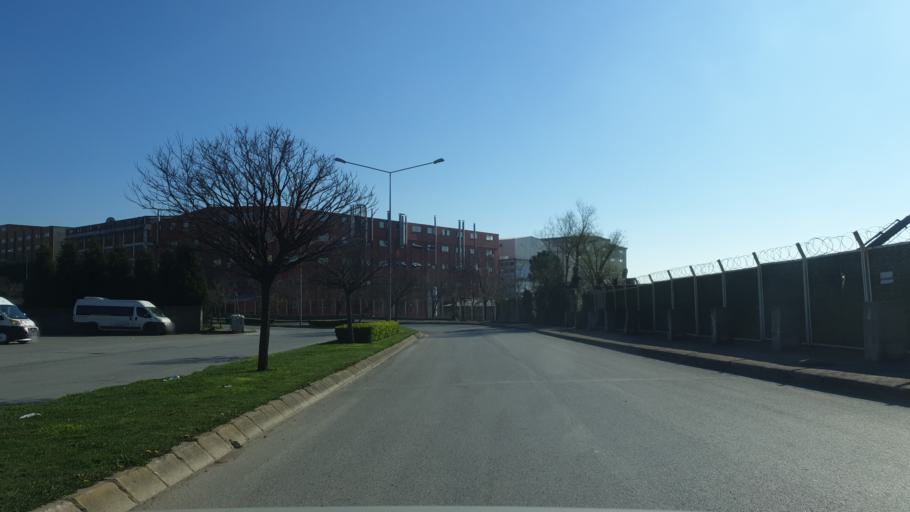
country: TR
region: Kocaeli
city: Balcik
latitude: 40.8787
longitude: 29.3714
